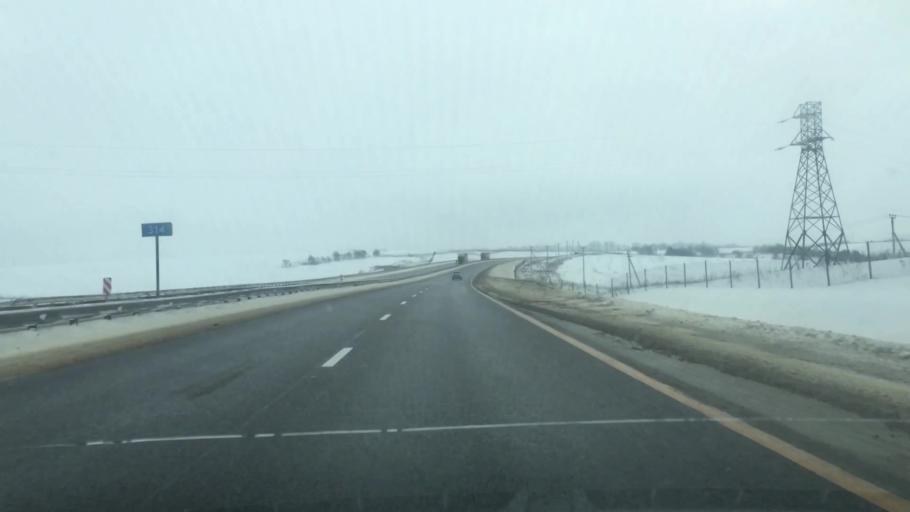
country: RU
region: Tula
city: Yefremov
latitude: 53.1441
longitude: 38.2482
